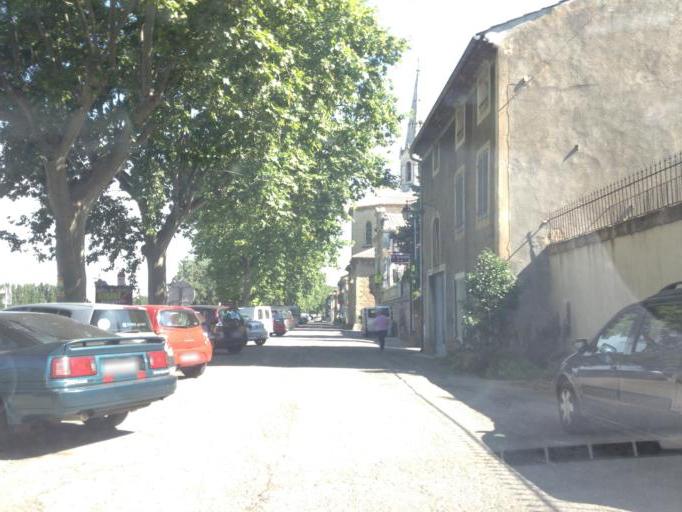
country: FR
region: Provence-Alpes-Cote d'Azur
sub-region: Departement du Vaucluse
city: Mornas
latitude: 44.2027
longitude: 4.7272
